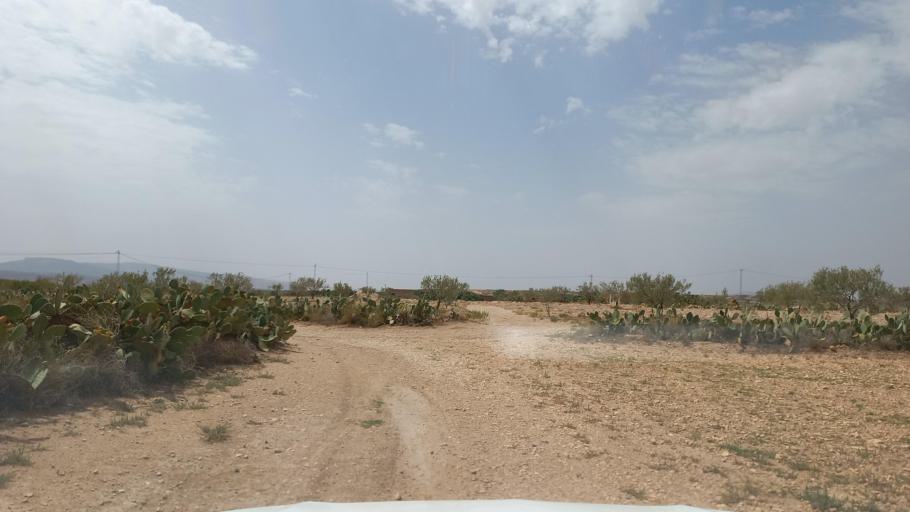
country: TN
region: Al Qasrayn
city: Kasserine
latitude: 35.2899
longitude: 9.0053
